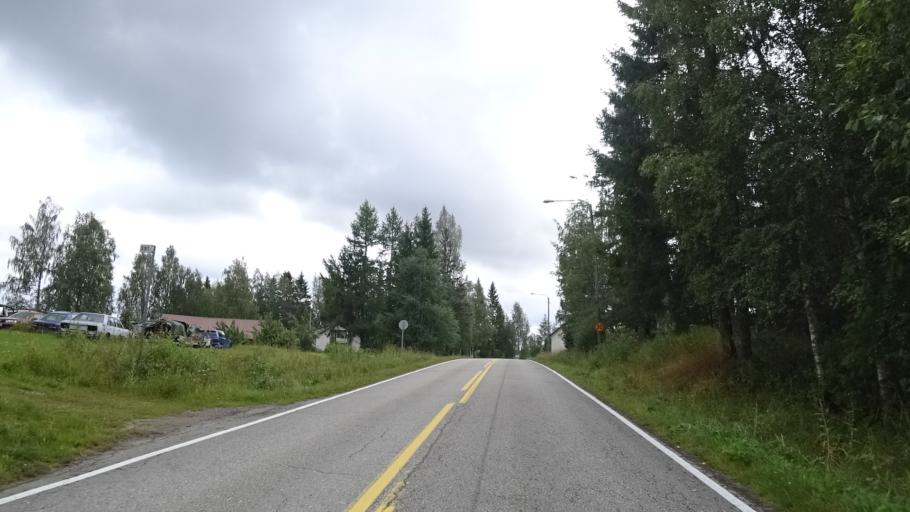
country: FI
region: North Karelia
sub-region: Joensuu
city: Ilomantsi
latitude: 62.9337
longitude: 31.2822
